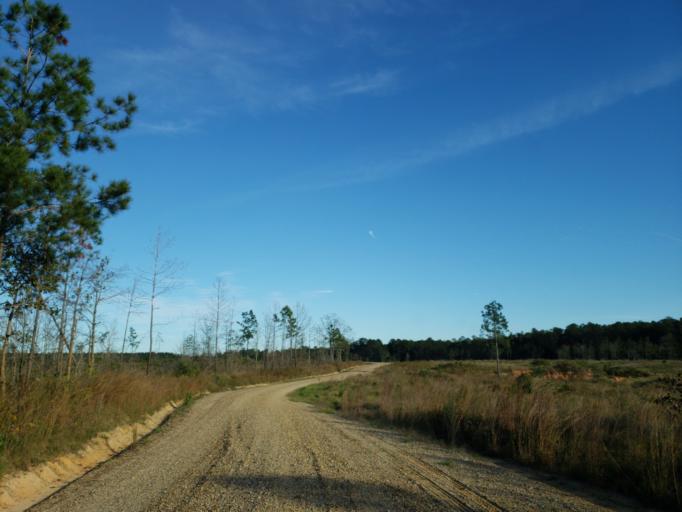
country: US
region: Mississippi
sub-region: Perry County
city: Richton
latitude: 31.3460
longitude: -88.8003
